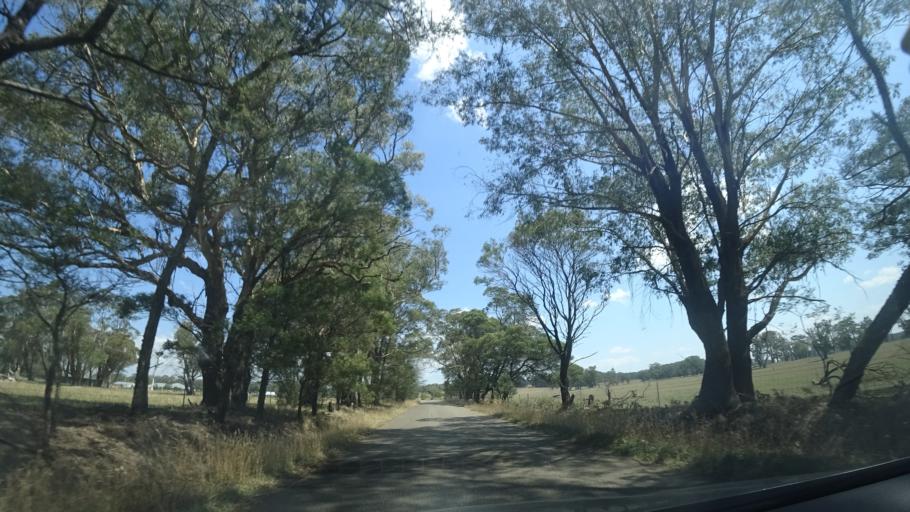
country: AU
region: New South Wales
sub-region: Wingecarribee
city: Bundanoon
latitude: -34.6119
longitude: 150.2780
